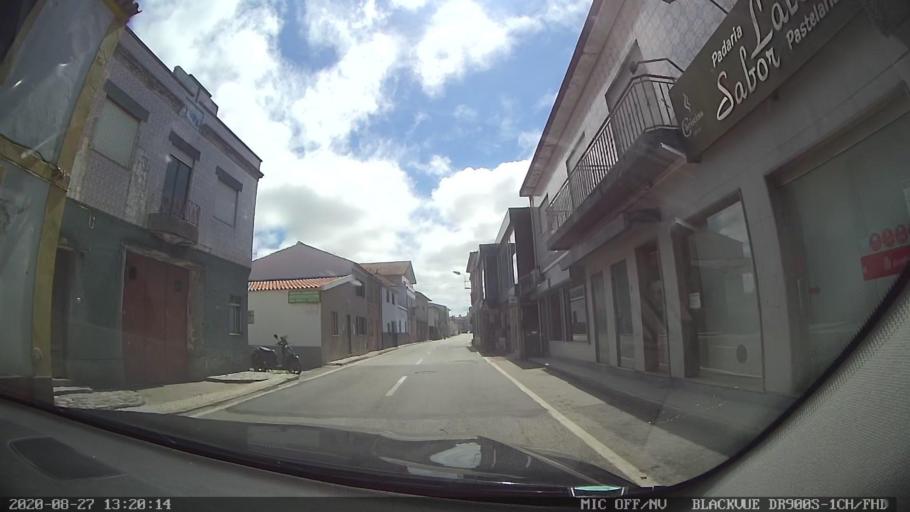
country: PT
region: Aveiro
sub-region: Vagos
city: Vagos
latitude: 40.5582
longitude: -8.6821
